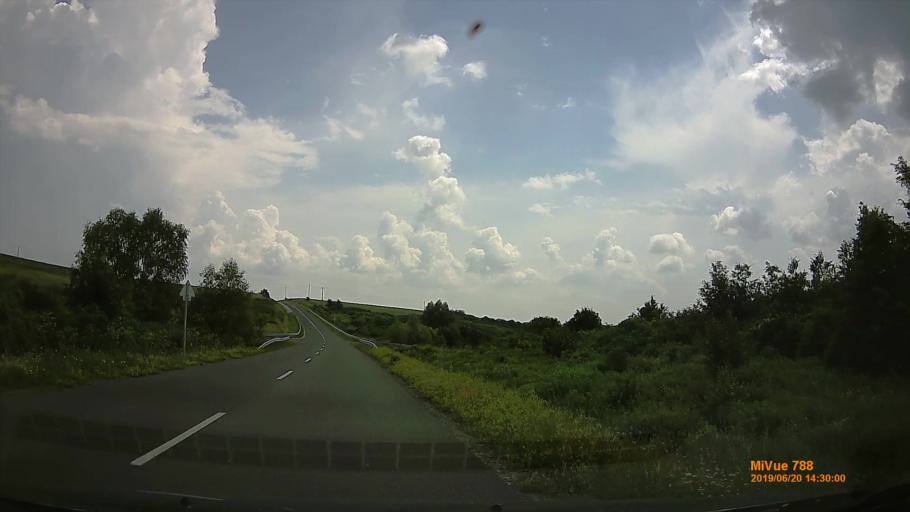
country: HU
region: Baranya
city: Hosszuheteny
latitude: 46.1536
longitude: 18.3434
